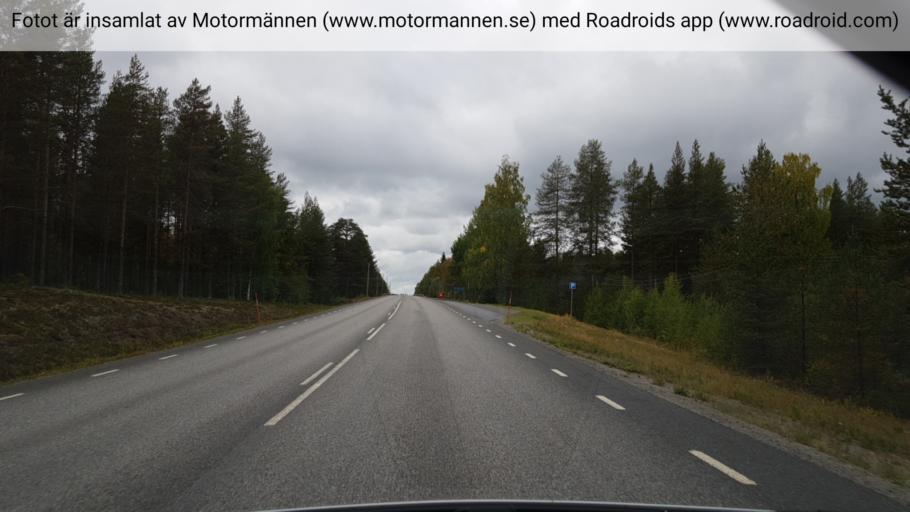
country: SE
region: Vaesterbotten
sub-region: Skelleftea Kommun
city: Langsele
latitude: 64.9321
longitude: 19.9827
